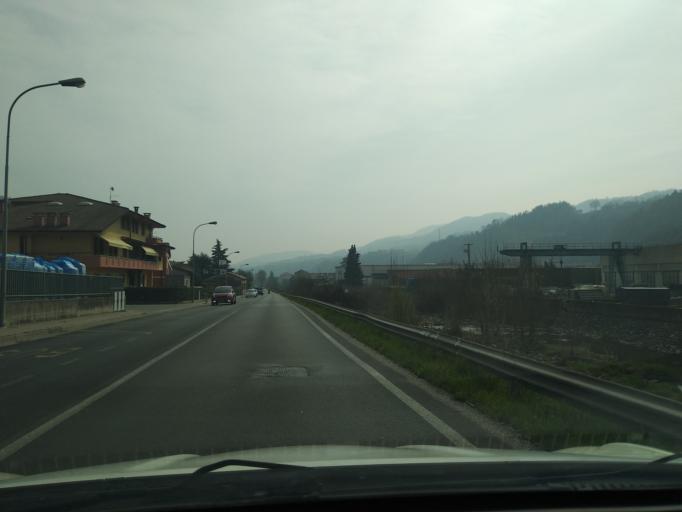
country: IT
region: Veneto
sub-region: Provincia di Vicenza
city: Chiampo
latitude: 45.5549
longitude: 11.2723
